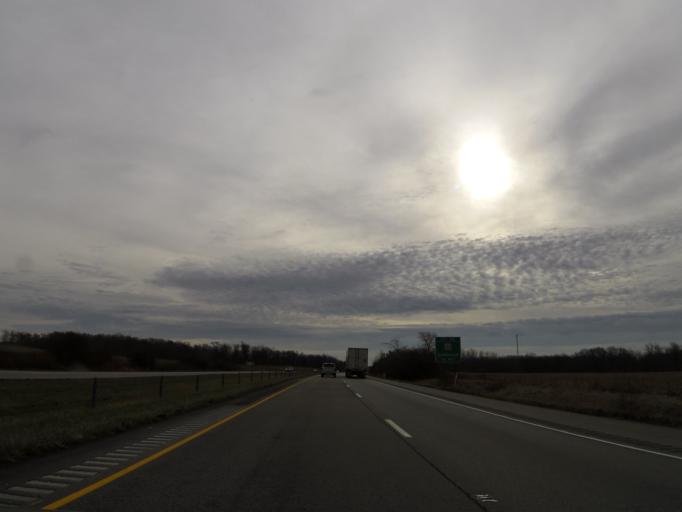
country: US
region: Indiana
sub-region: Montgomery County
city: Crawfordsville
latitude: 40.0555
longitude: -86.8232
